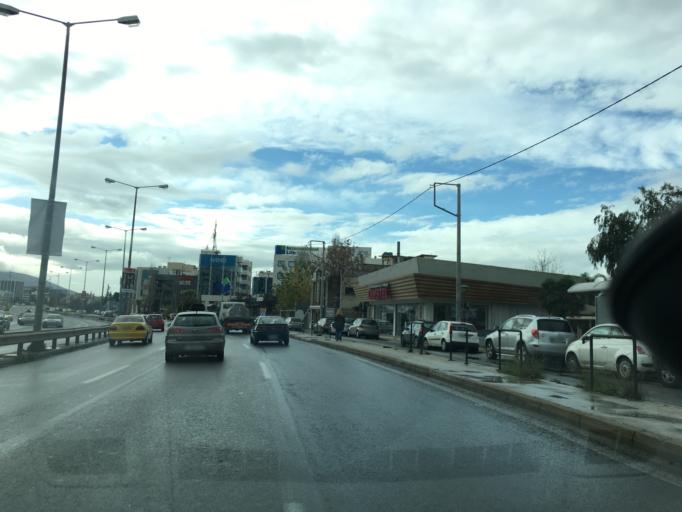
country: GR
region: Attica
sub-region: Nomarchia Athinas
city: Filothei
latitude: 38.0273
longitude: 23.7898
